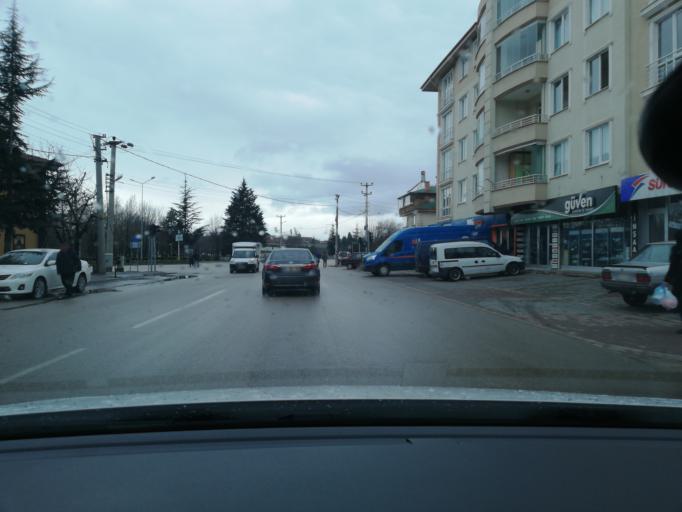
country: TR
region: Bolu
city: Bolu
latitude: 40.7409
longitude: 31.6161
